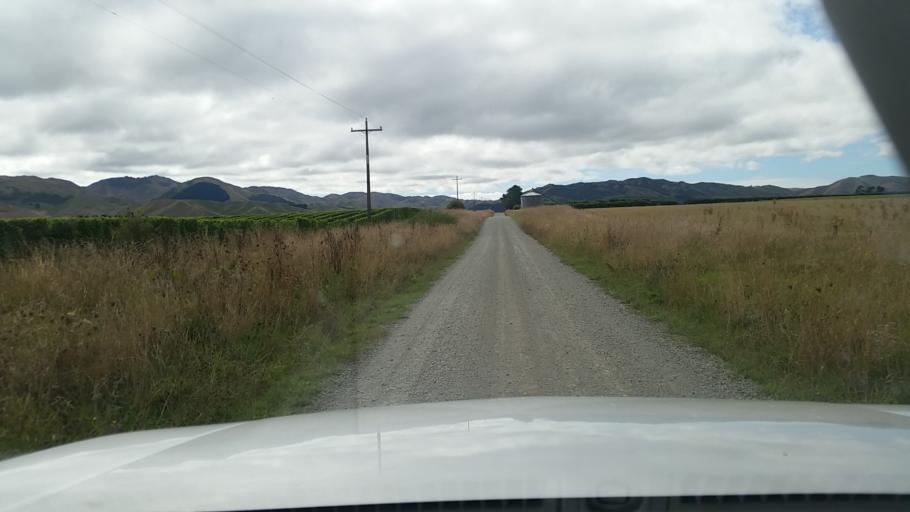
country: NZ
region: Marlborough
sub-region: Marlborough District
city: Blenheim
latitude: -41.6815
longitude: 174.0387
